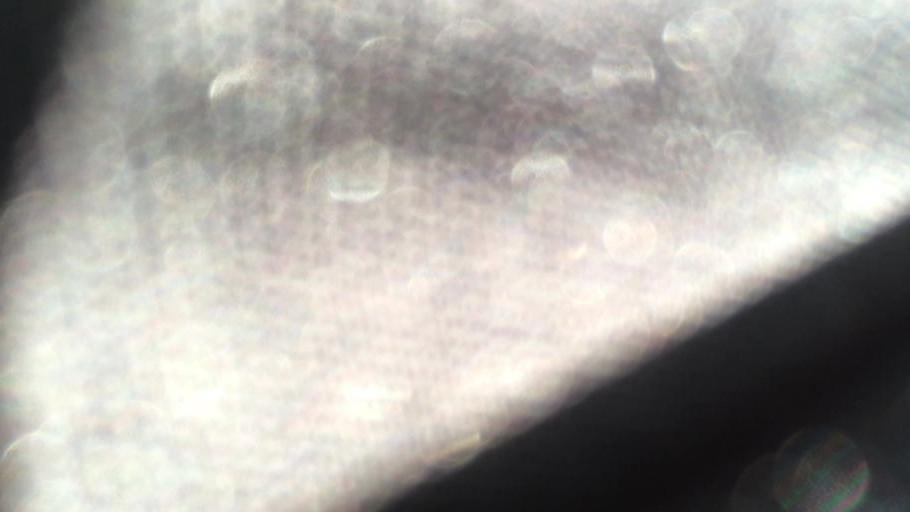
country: US
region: Maryland
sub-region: Somerset County
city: Princess Anne
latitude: 38.1739
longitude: -75.6894
